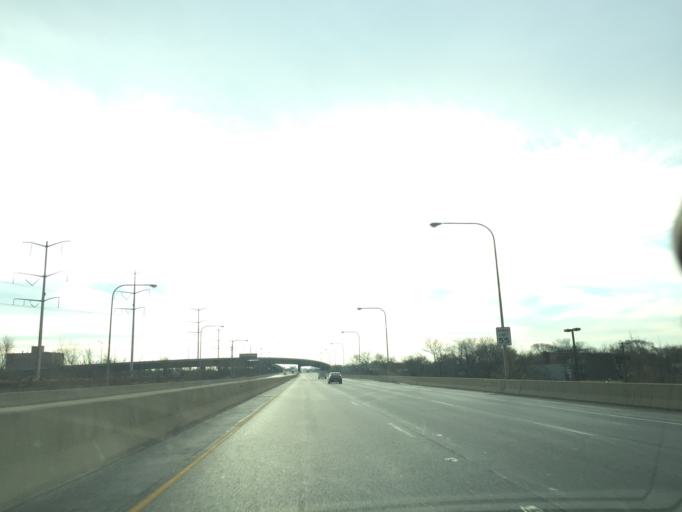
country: US
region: Illinois
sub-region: Cook County
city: Calumet Park
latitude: 41.7524
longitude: -87.5896
